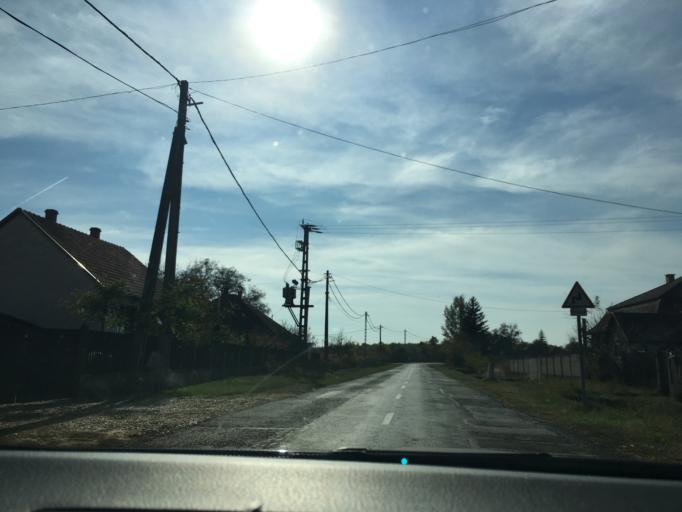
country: HU
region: Hajdu-Bihar
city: Nyirabrany
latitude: 47.5407
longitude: 22.0101
